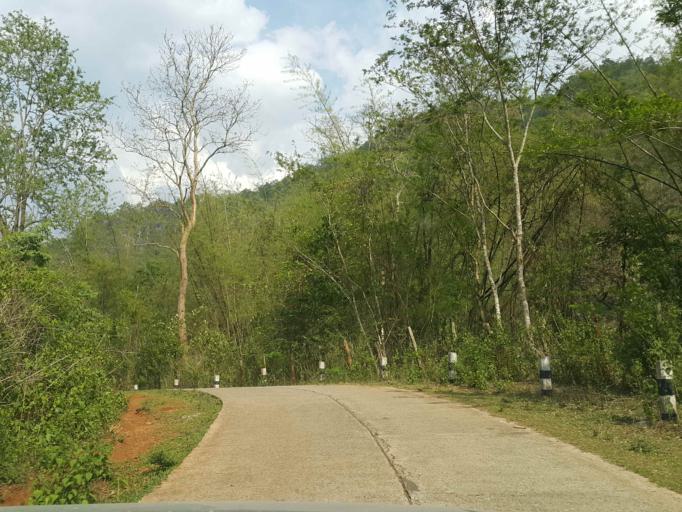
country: TH
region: Chiang Mai
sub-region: Amphoe Chiang Dao
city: Chiang Dao
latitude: 19.4008
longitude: 98.7784
